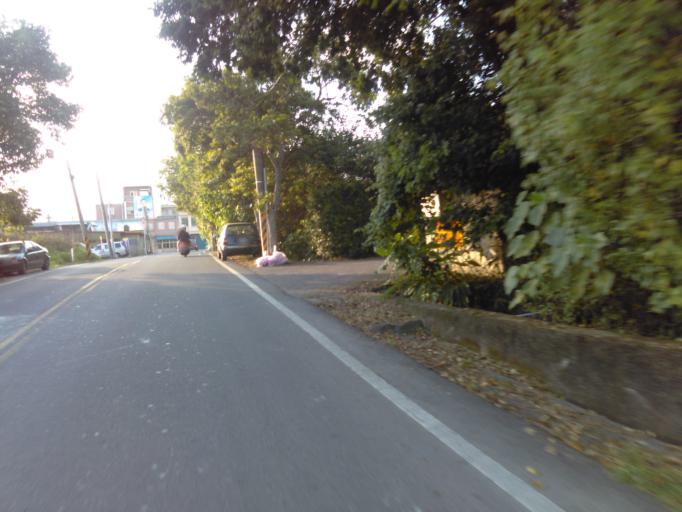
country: TW
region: Taiwan
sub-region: Yilan
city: Yilan
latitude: 24.8088
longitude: 121.7681
